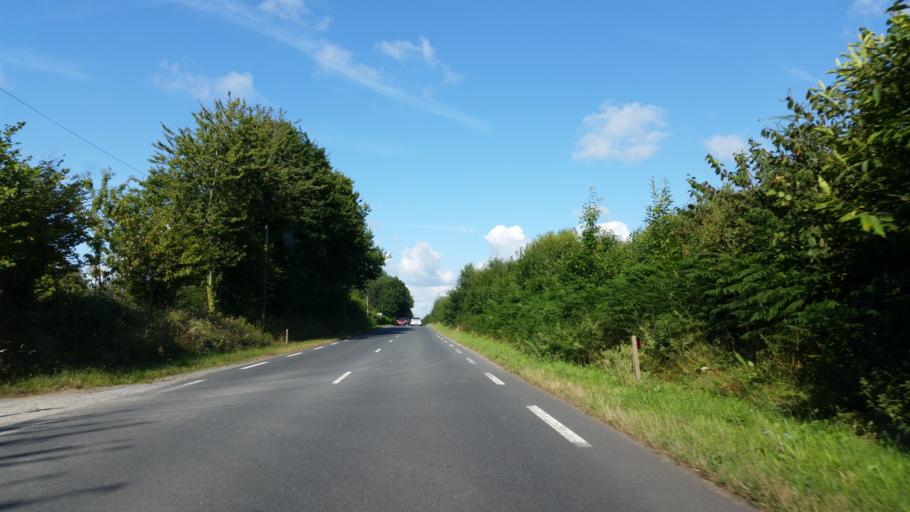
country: FR
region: Lower Normandy
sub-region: Departement du Calvados
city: Saint-Gatien-des-Bois
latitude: 49.3436
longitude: 0.1435
